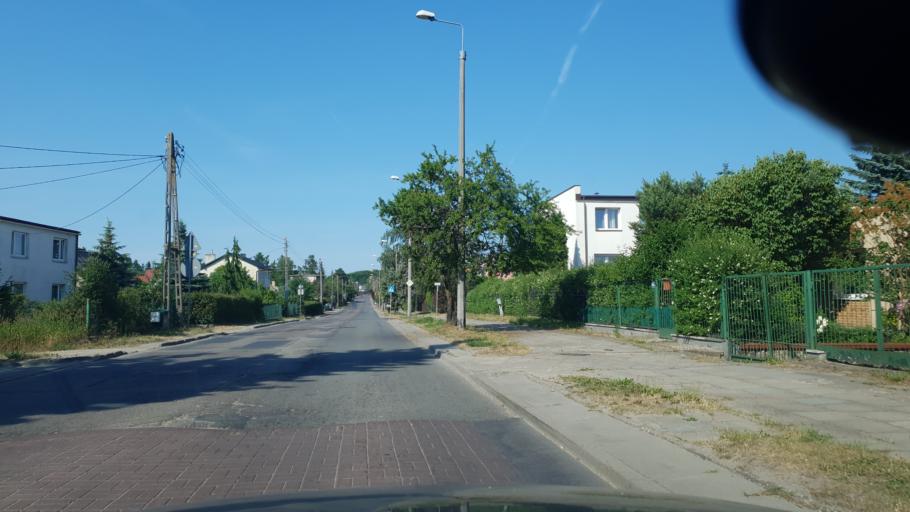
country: PL
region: Pomeranian Voivodeship
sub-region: Gdynia
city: Wielki Kack
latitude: 54.4303
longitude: 18.4622
